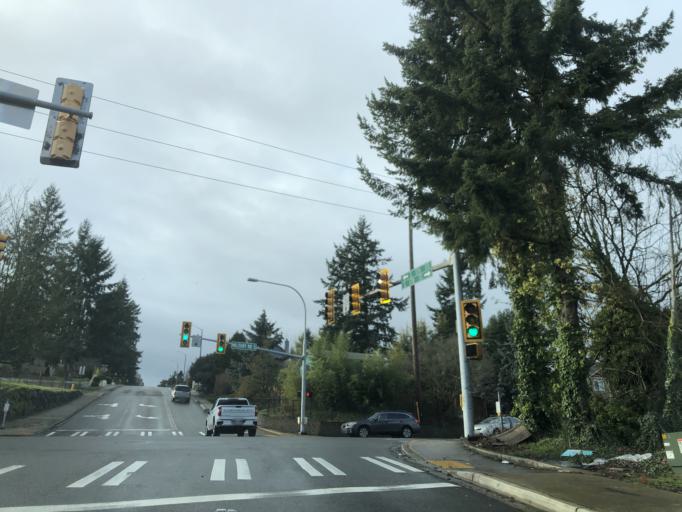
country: US
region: Washington
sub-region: King County
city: SeaTac
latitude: 47.4451
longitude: -122.2745
